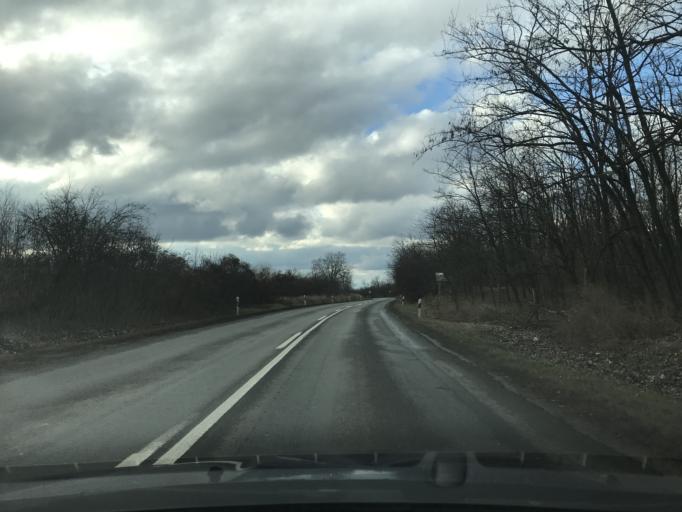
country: HU
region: Bacs-Kiskun
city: Nemesnadudvar
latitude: 46.3408
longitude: 19.0729
